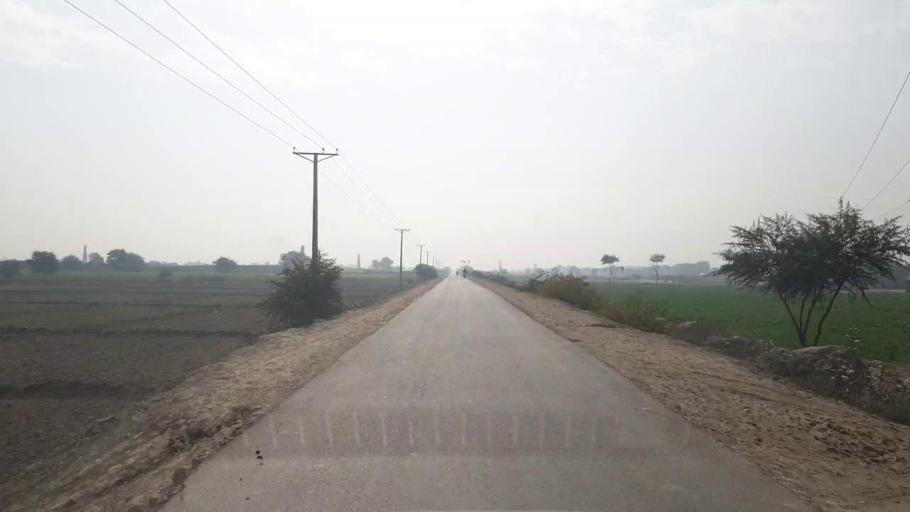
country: PK
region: Sindh
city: Hala
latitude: 25.7792
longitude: 68.4436
